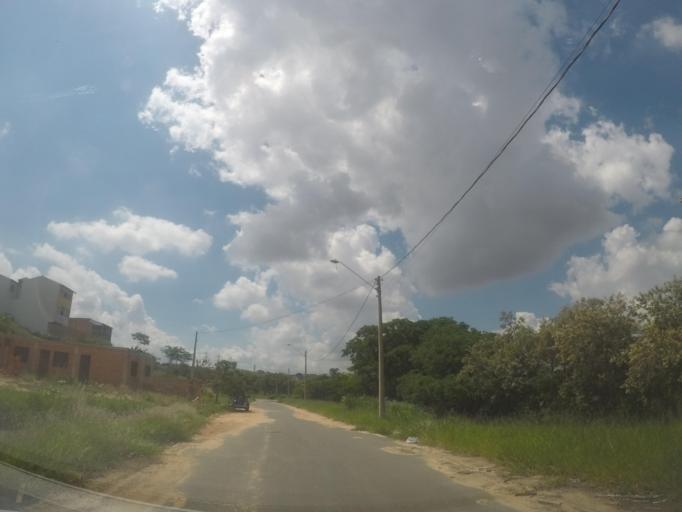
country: BR
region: Sao Paulo
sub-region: Hortolandia
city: Hortolandia
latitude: -22.8410
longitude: -47.2038
